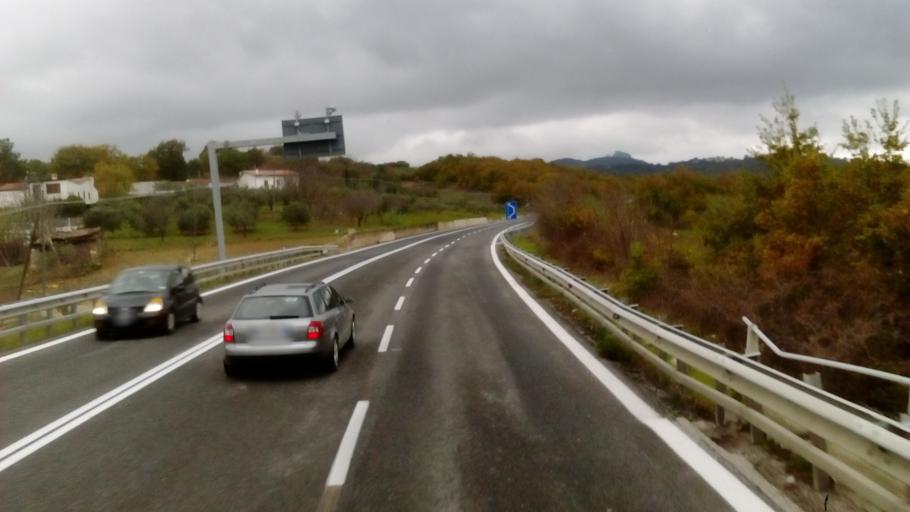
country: IT
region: Molise
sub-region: Provincia di Isernia
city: Bagnoli del Trigno
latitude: 41.7265
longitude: 14.4450
